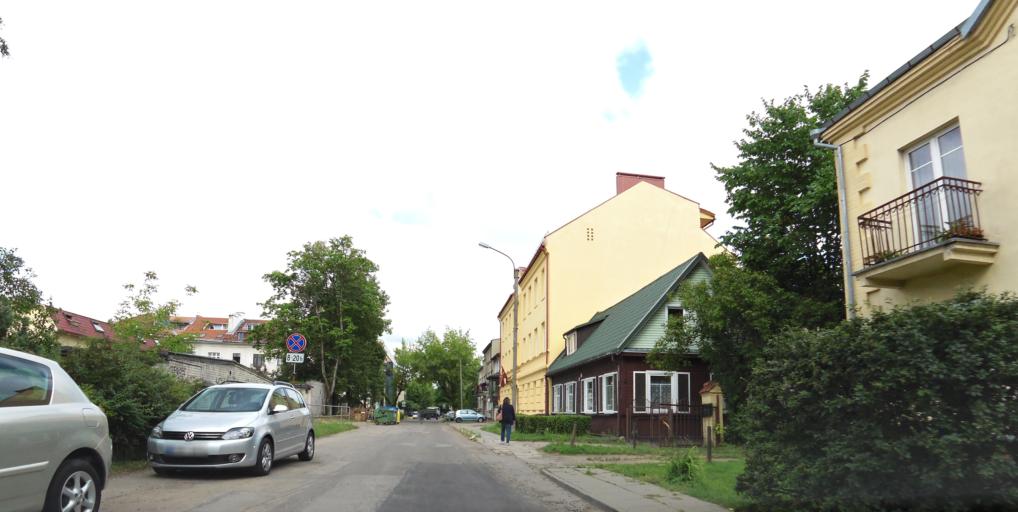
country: LT
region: Vilnius County
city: Naujamiestis
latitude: 54.6895
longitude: 25.2539
